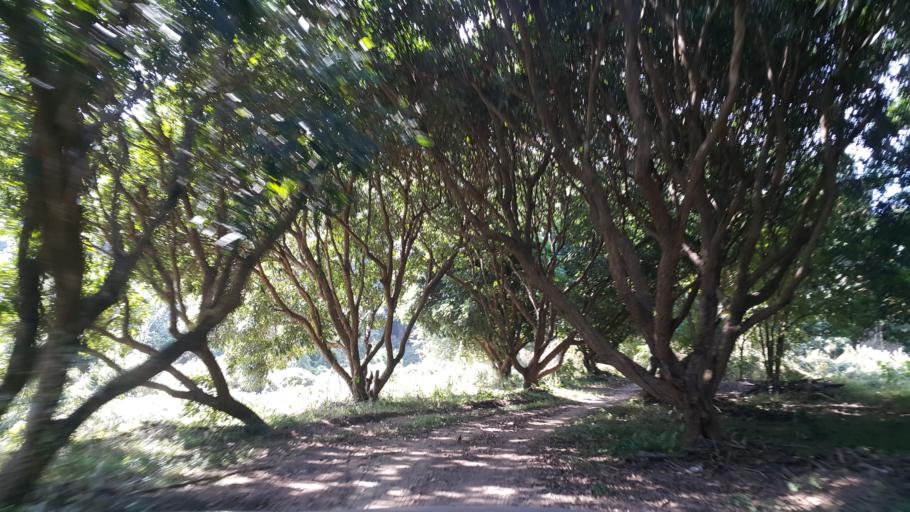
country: TH
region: Lamphun
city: Ban Thi
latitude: 18.5716
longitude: 99.1741
